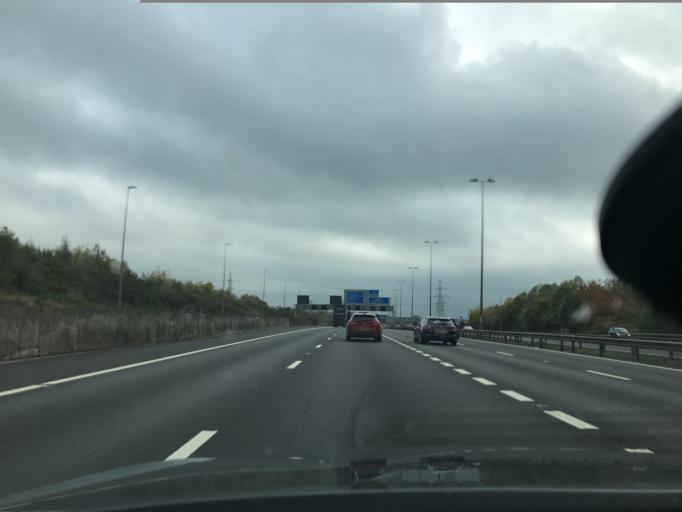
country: GB
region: England
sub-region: Warwickshire
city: Water Orton
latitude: 52.5042
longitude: -1.7225
